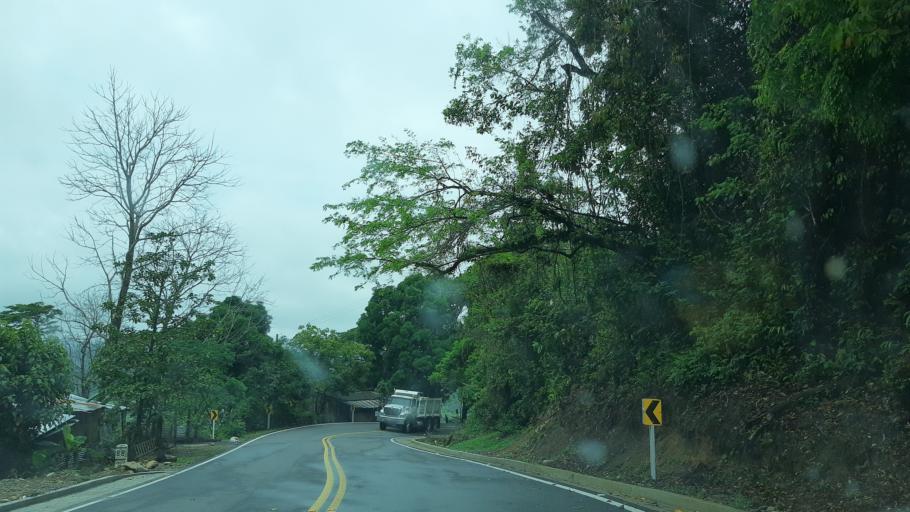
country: CO
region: Casanare
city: Sabanalarga
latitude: 4.7640
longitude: -73.0292
